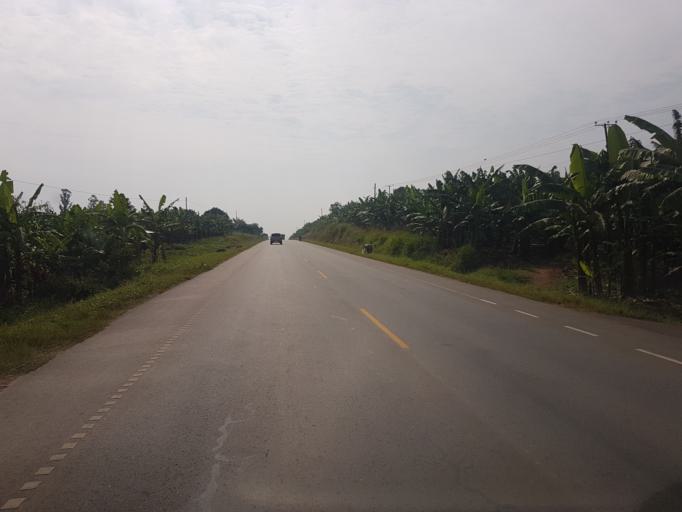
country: UG
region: Western Region
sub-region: Sheema District
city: Kibingo
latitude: -0.6385
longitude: 30.5120
